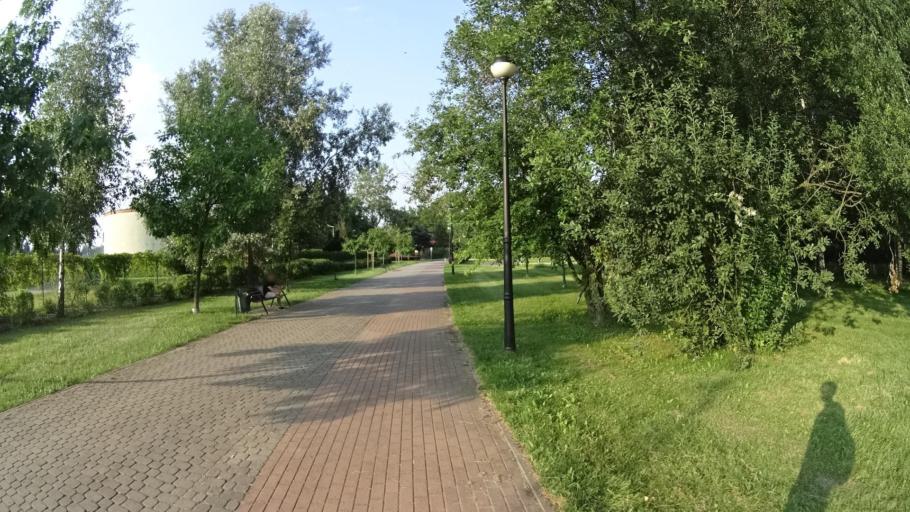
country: PL
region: Masovian Voivodeship
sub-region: Powiat pruszkowski
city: Rybie
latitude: 52.1482
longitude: 20.9296
